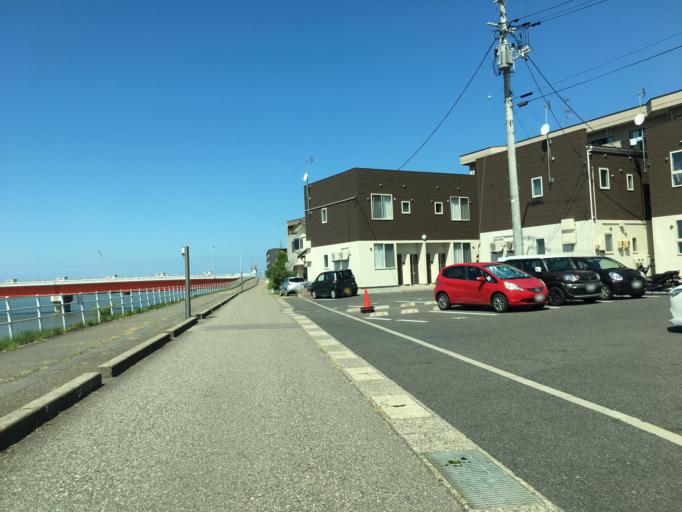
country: JP
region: Niigata
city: Niigata-shi
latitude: 37.9043
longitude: 139.0078
